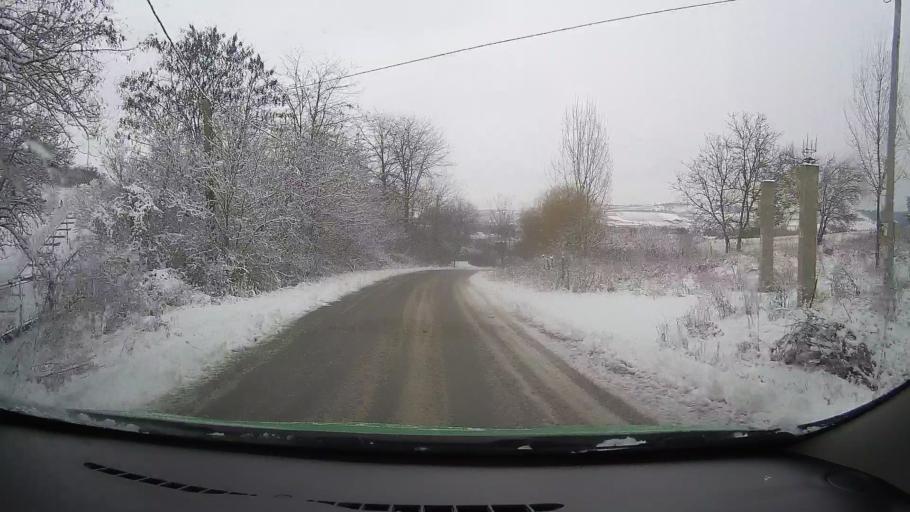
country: RO
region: Hunedoara
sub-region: Municipiul Hunedoara
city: Pestisu Mare
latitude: 45.8038
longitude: 22.9208
